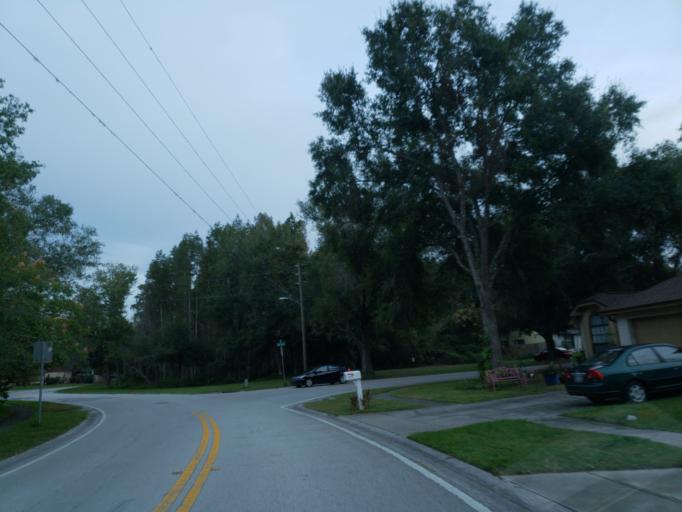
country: US
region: Florida
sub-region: Hillsborough County
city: Lutz
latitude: 28.1802
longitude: -82.4599
